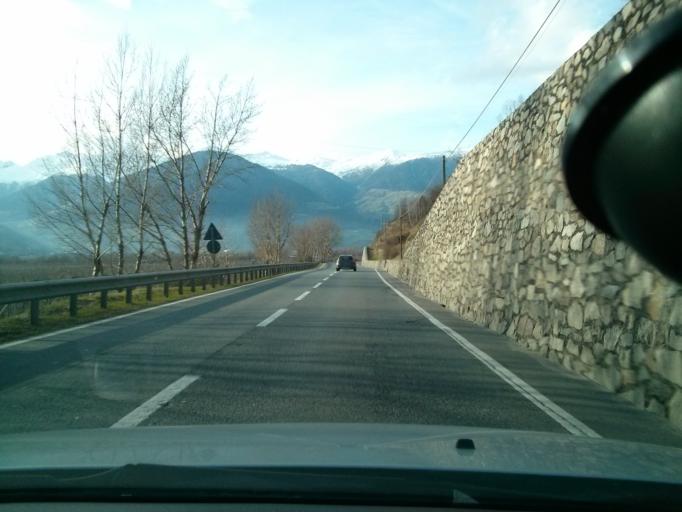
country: IT
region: Trentino-Alto Adige
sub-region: Bolzano
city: Prato Allo Stelvio
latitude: 46.6309
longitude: 10.6318
